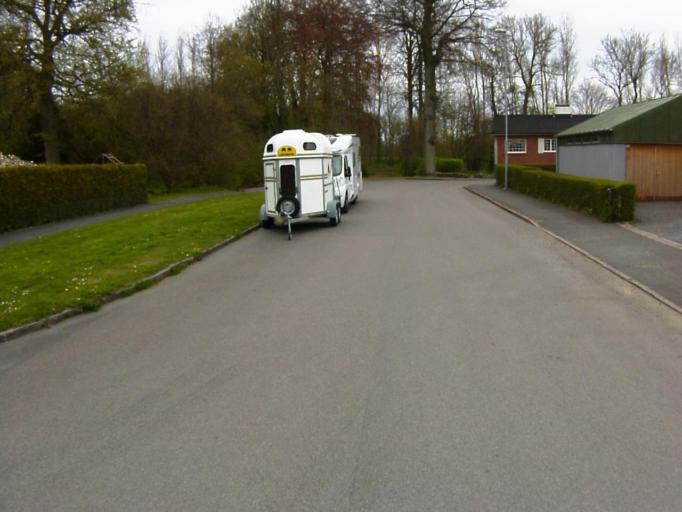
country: SE
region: Skane
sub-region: Kristianstads Kommun
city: Kristianstad
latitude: 56.0194
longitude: 14.1623
